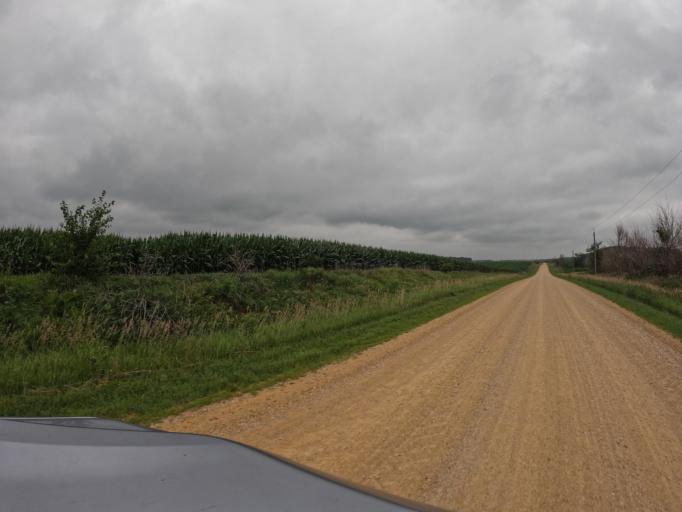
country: US
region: Illinois
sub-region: Carroll County
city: Savanna
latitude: 41.9822
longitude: -90.1919
